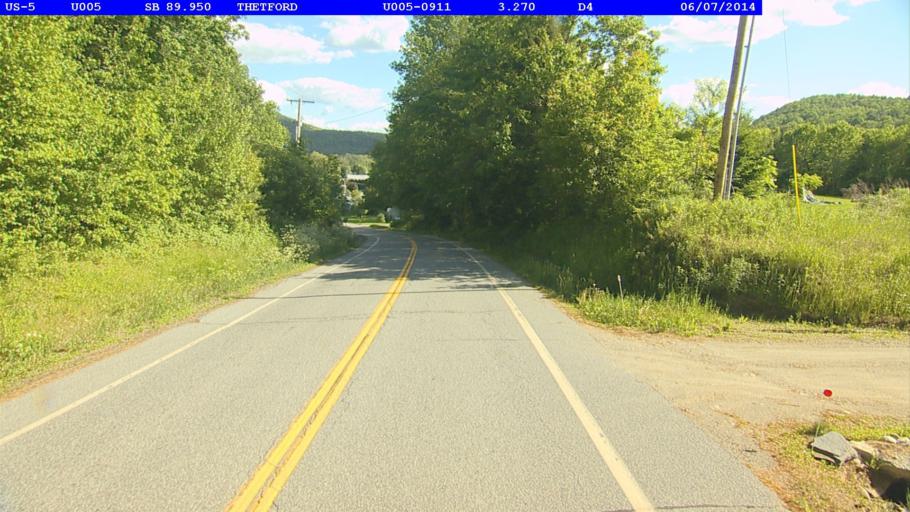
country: US
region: New Hampshire
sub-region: Grafton County
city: Lyme
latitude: 43.8155
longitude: -72.1902
